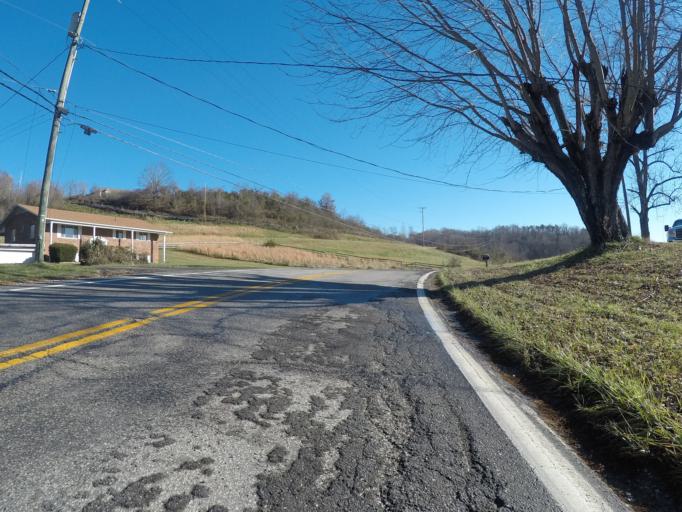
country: US
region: West Virginia
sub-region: Cabell County
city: Huntington
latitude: 38.4867
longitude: -82.4654
